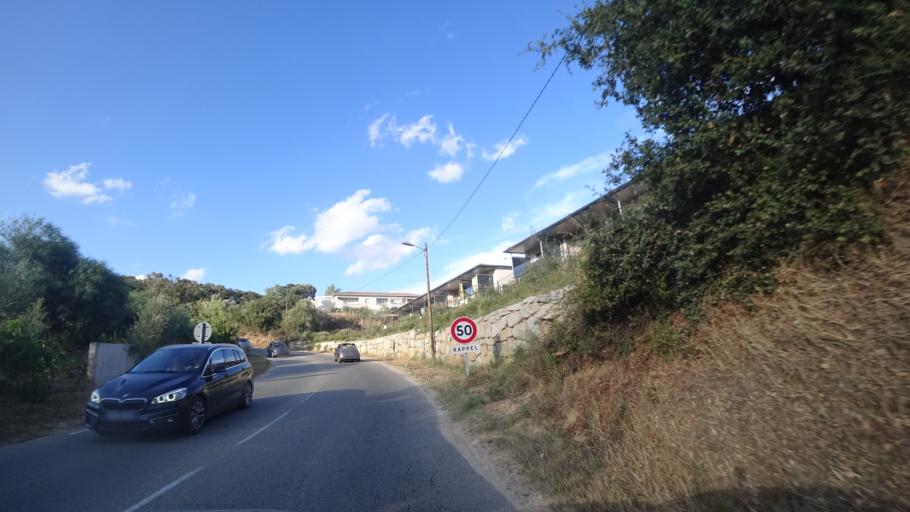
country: FR
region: Corsica
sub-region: Departement de la Corse-du-Sud
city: Ajaccio
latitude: 41.9454
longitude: 8.7368
